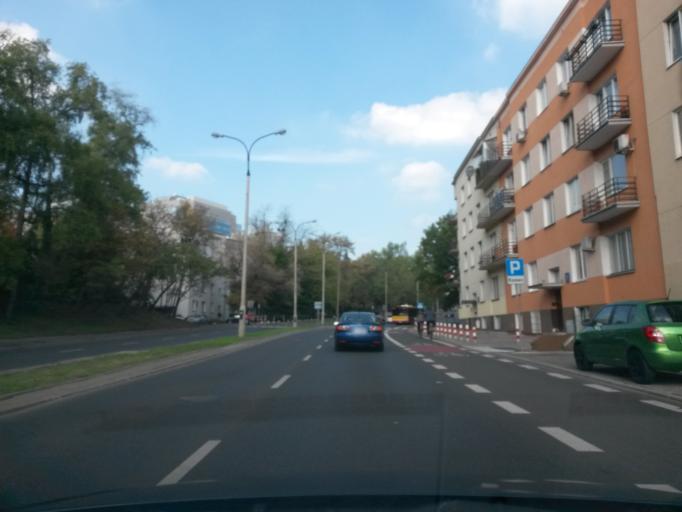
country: PL
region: Masovian Voivodeship
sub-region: Warszawa
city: Mokotow
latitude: 52.2090
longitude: 21.0264
